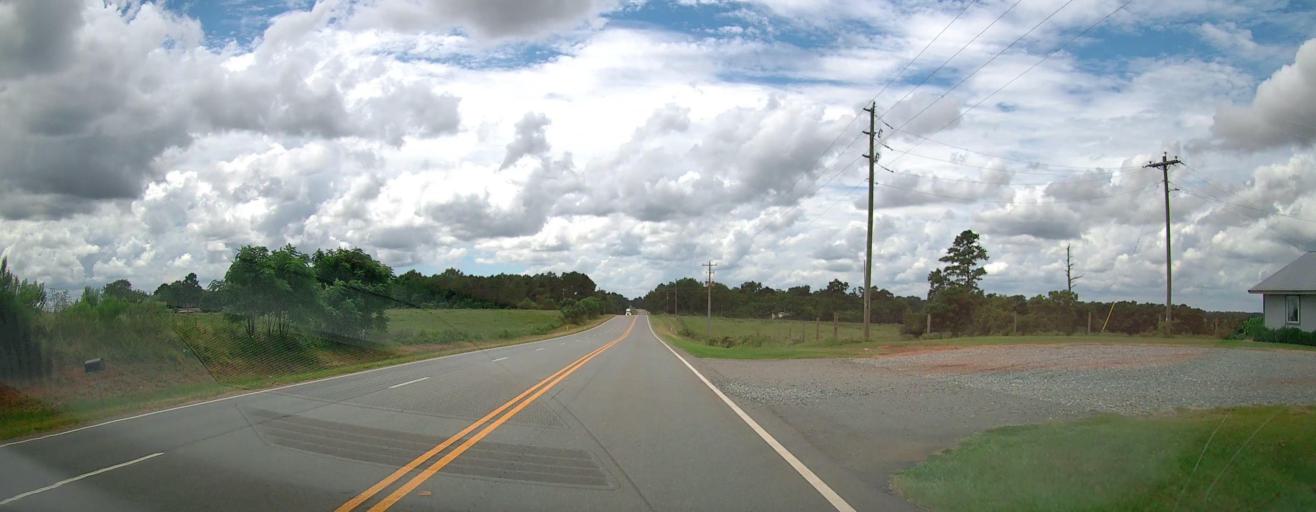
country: US
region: Georgia
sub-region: Macon County
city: Montezuma
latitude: 32.2923
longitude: -83.9348
